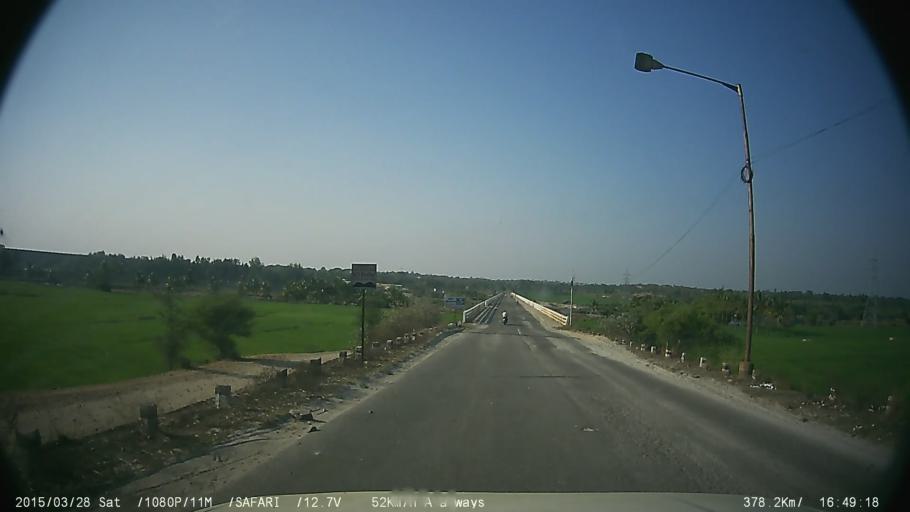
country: IN
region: Karnataka
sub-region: Mandya
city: Shrirangapattana
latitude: 12.4198
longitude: 76.5810
